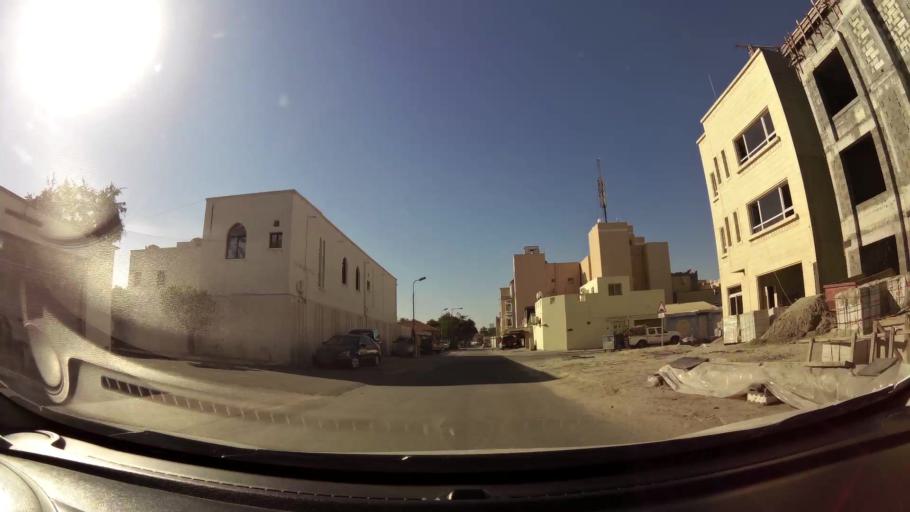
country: BH
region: Muharraq
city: Al Muharraq
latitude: 26.2596
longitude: 50.6069
